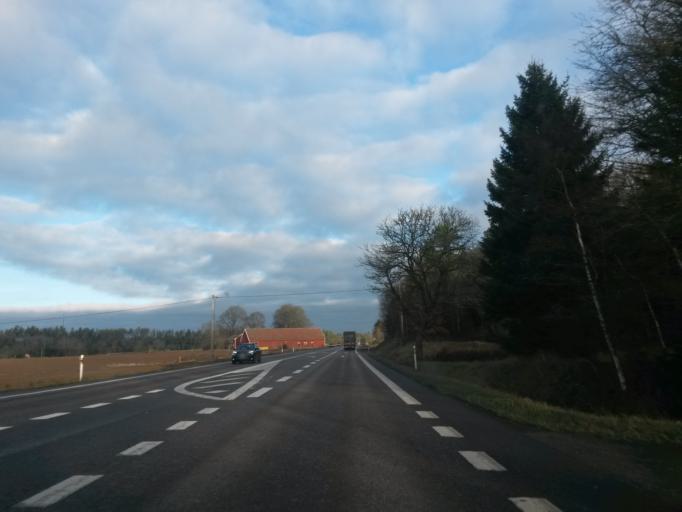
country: SE
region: Vaestra Goetaland
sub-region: Vargarda Kommun
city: Vargarda
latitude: 58.0793
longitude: 12.8168
